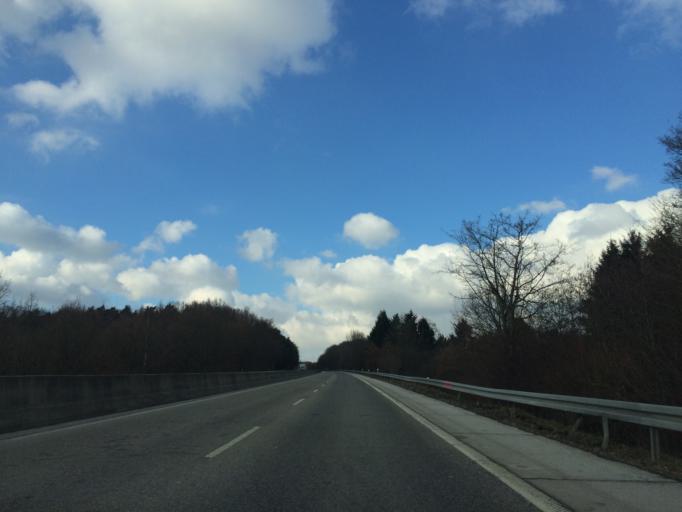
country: DE
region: Hesse
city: Liederbach
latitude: 50.1420
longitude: 8.4800
